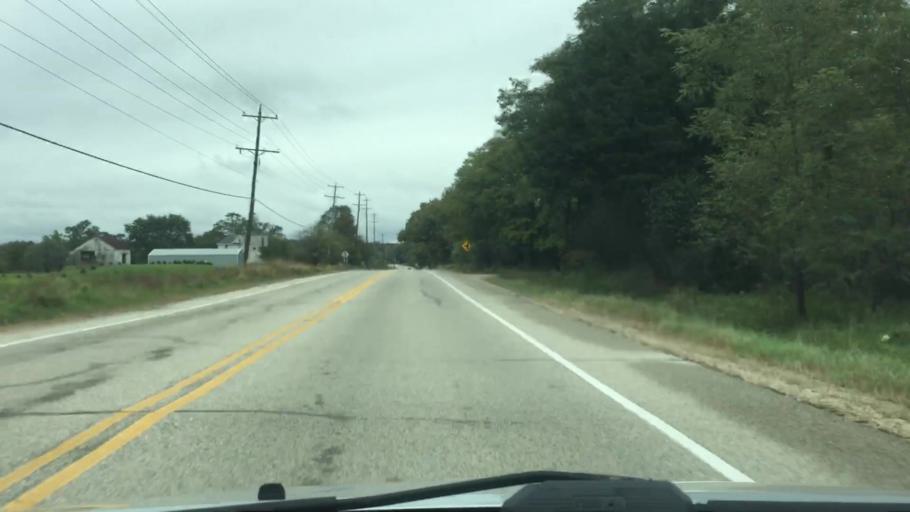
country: US
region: Wisconsin
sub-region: Waukesha County
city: Eagle
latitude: 42.8573
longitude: -88.4919
